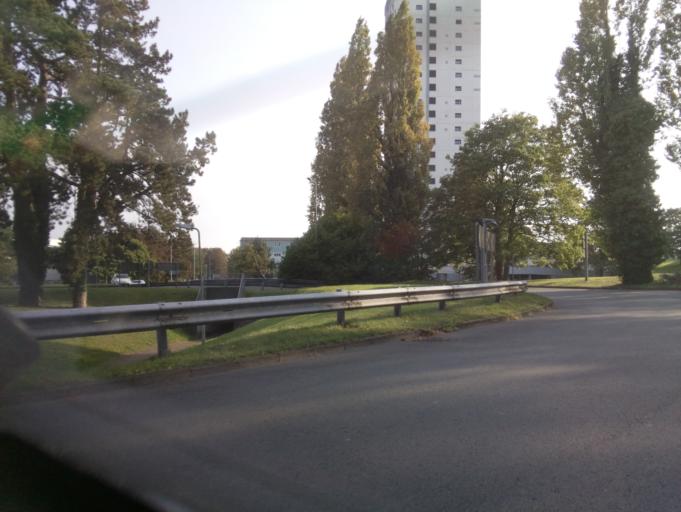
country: GB
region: Wales
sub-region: Torfaen County Borough
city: Cwmbran
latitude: 51.6520
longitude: -3.0191
